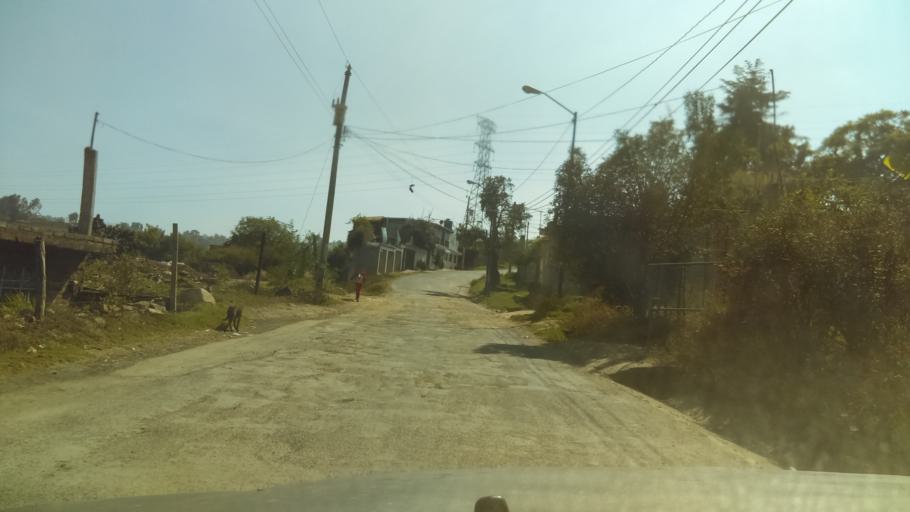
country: MX
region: Michoacan
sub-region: Morelia
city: Montana Monarca (Punta Altozano)
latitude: 19.6577
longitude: -101.1817
